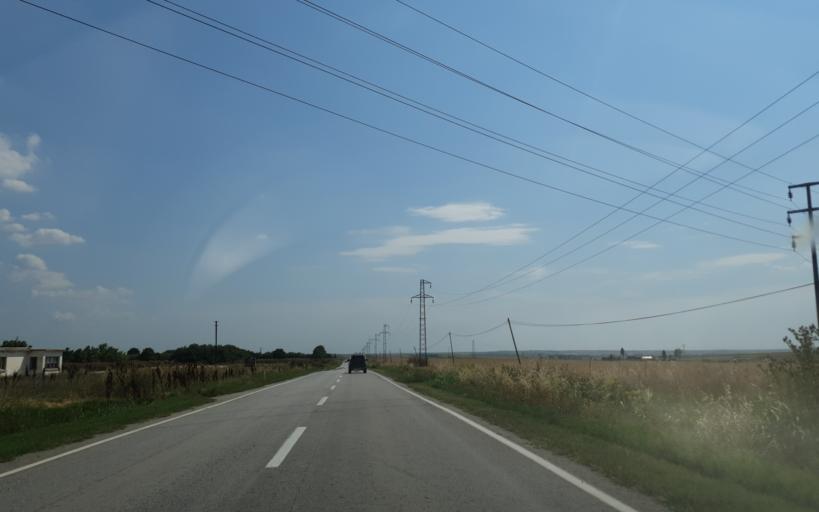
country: TR
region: Kirklareli
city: Buyukkaristiran
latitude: 41.3160
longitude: 27.5201
